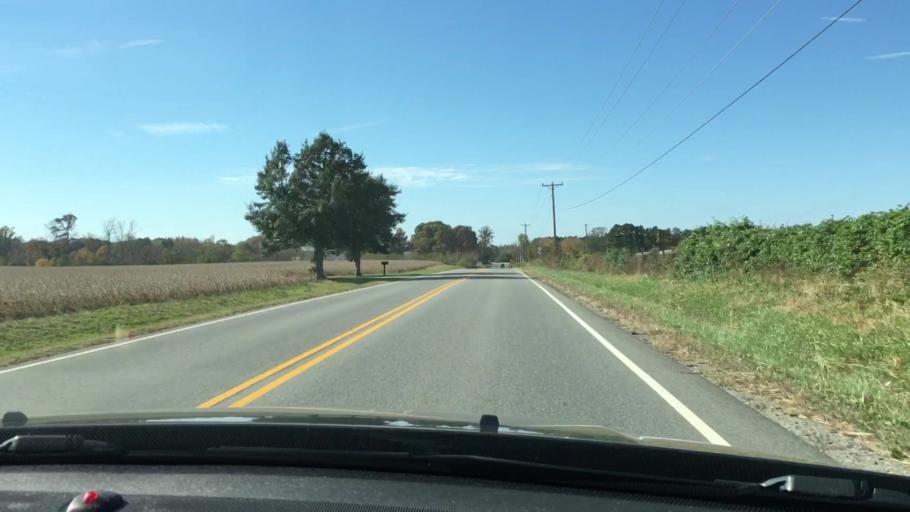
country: US
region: Virginia
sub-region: King and Queen County
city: King and Queen Court House
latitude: 37.5913
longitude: -76.8891
